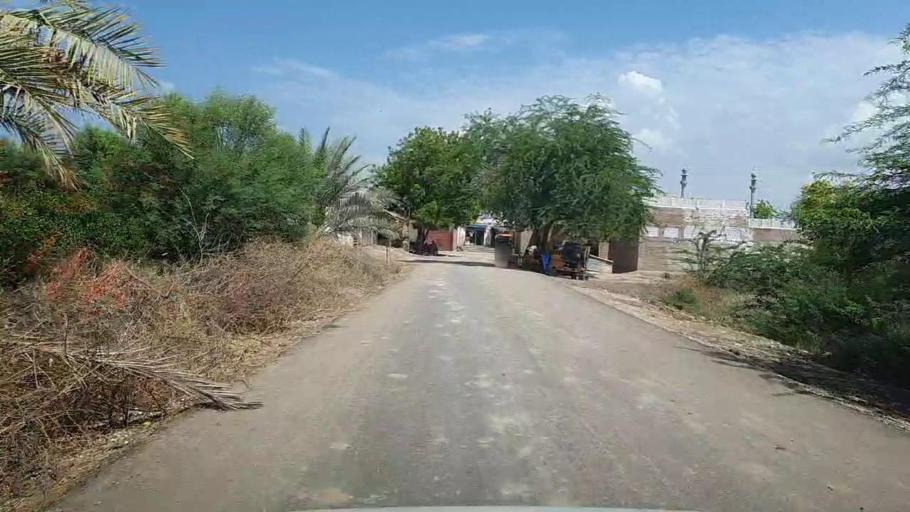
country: PK
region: Sindh
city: Bhiria
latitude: 26.9509
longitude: 68.2302
